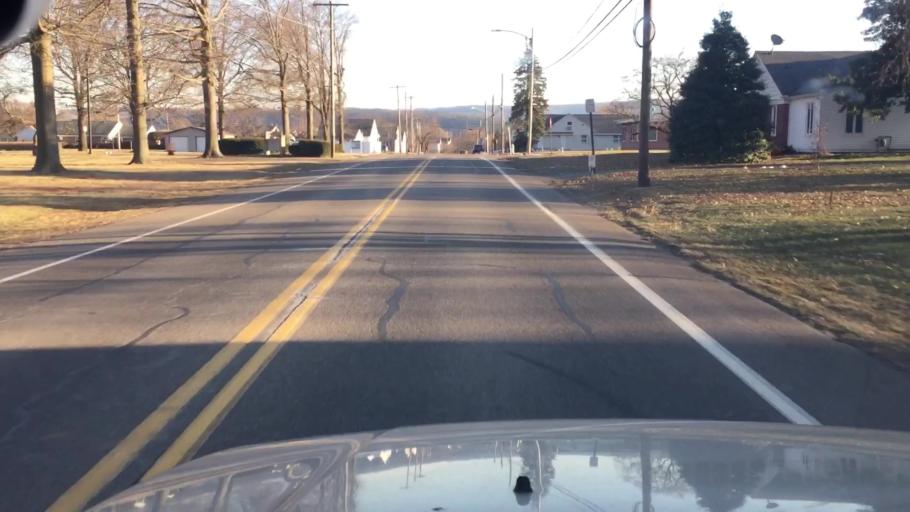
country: US
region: Pennsylvania
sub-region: Luzerne County
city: East Berwick
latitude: 41.0662
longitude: -76.2305
